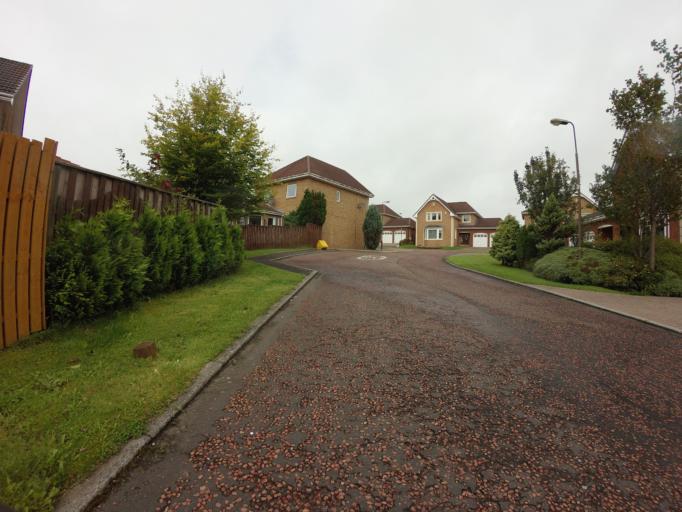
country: GB
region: Scotland
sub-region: West Lothian
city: Livingston
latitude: 55.9126
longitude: -3.5358
